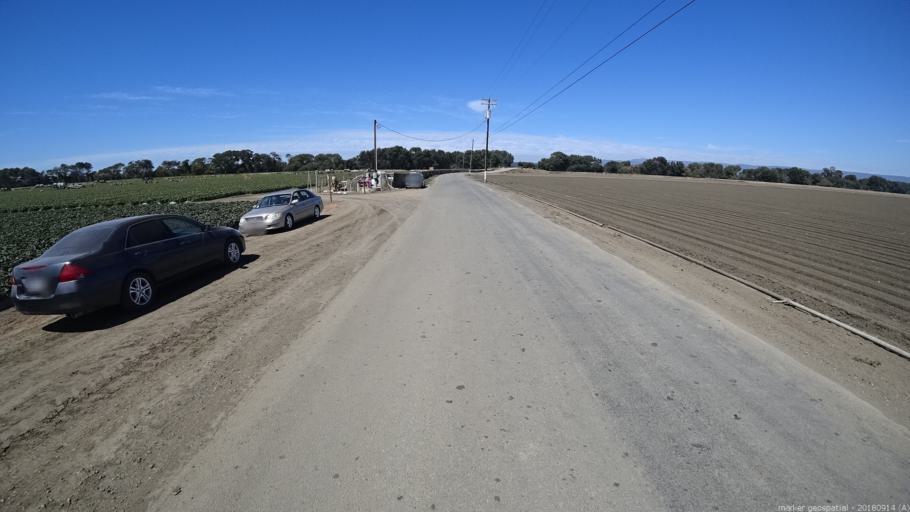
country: US
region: California
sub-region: Santa Cruz County
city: Watsonville
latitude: 36.8765
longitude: -121.7908
